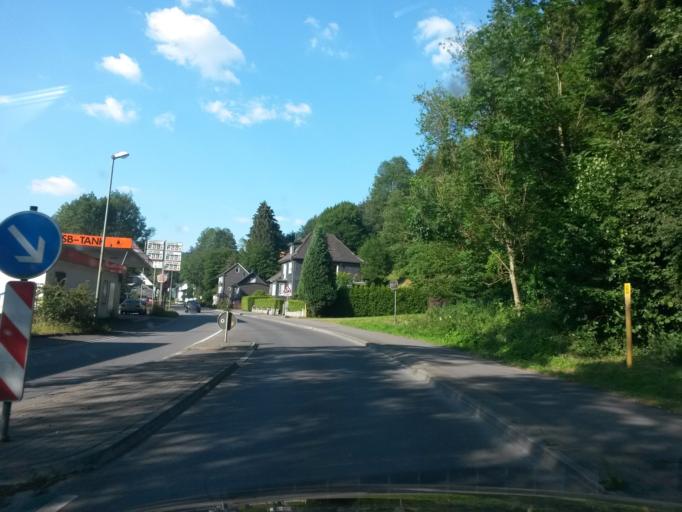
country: DE
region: North Rhine-Westphalia
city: Wiehl
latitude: 50.9877
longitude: 7.4888
